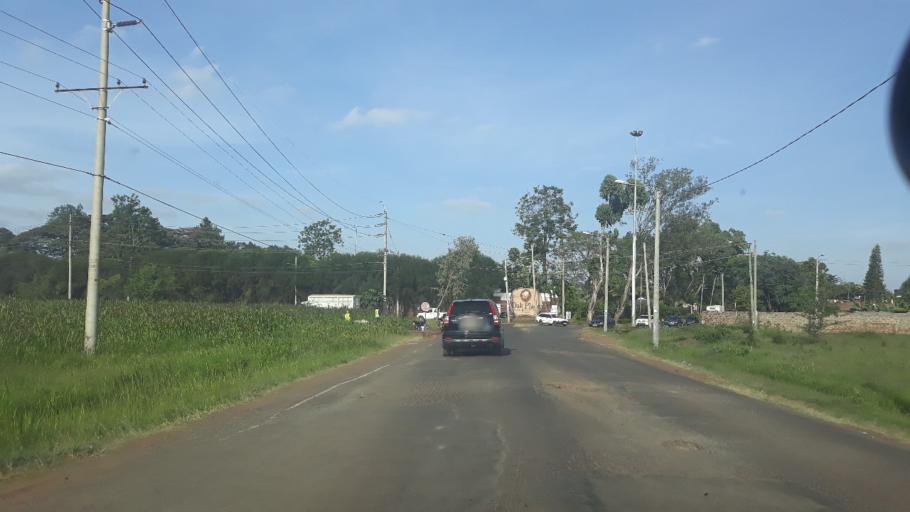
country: KE
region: Kiambu
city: Kiambu
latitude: -1.2186
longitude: 36.8510
